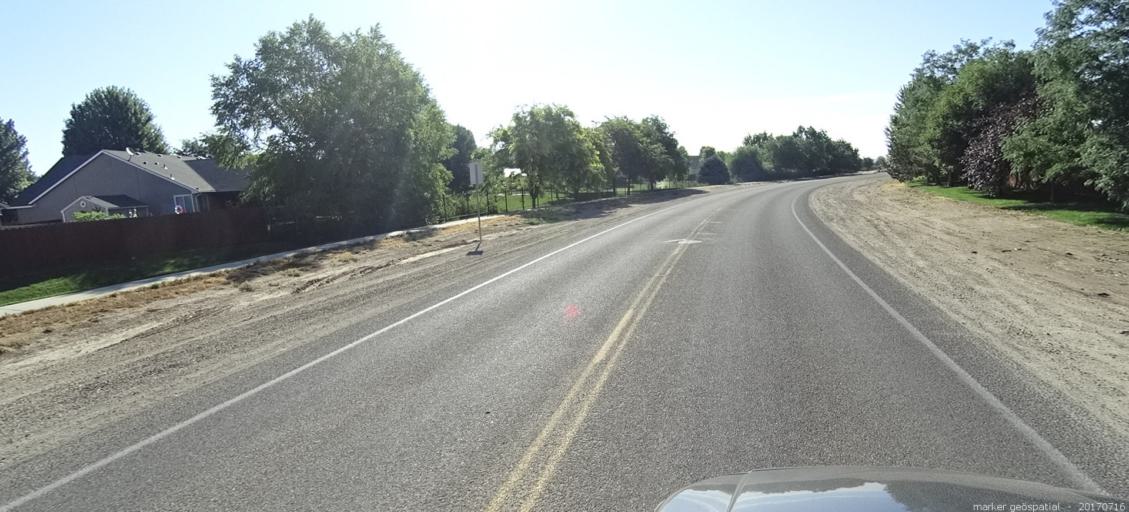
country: US
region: Idaho
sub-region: Ada County
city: Garden City
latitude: 43.5445
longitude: -116.2821
